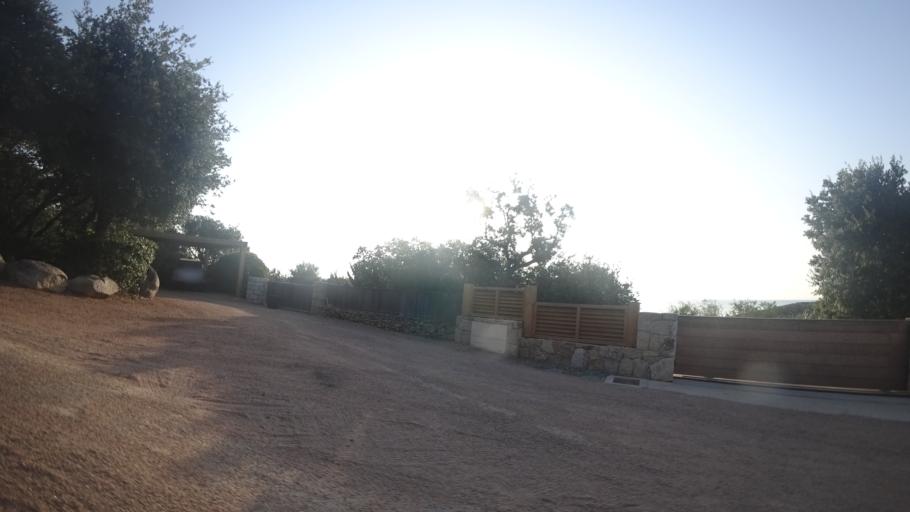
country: FR
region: Corsica
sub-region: Departement de la Corse-du-Sud
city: Porto-Vecchio
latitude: 41.6230
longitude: 9.3530
